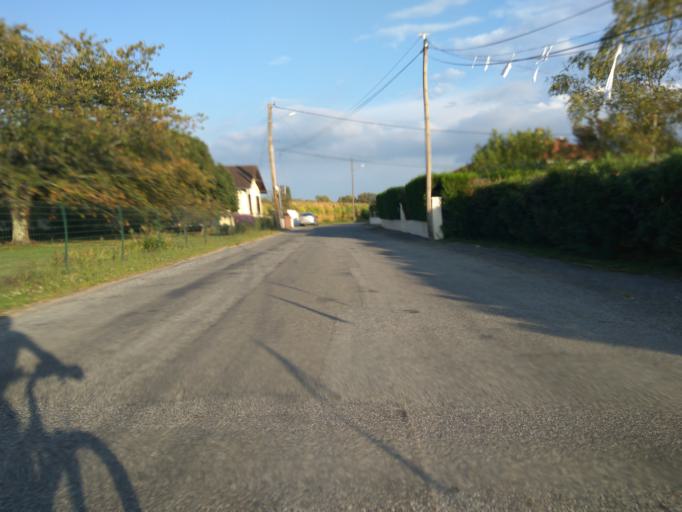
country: FR
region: Aquitaine
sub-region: Departement des Pyrenees-Atlantiques
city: Bizanos
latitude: 43.2806
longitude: -0.3541
